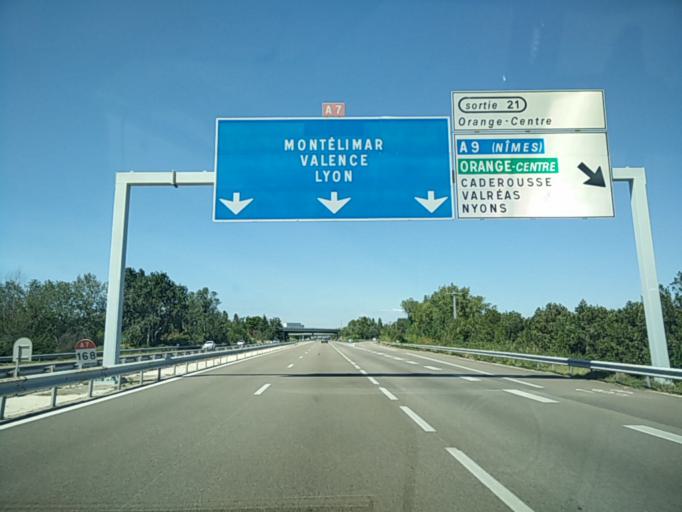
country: FR
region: Provence-Alpes-Cote d'Azur
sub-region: Departement du Vaucluse
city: Orange
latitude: 44.1261
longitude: 4.7955
